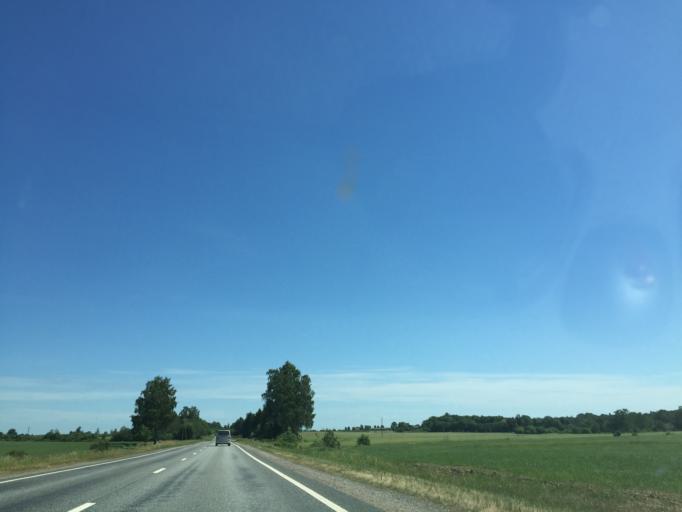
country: LV
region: Jaunpils
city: Jaunpils
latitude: 56.6550
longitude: 22.8788
